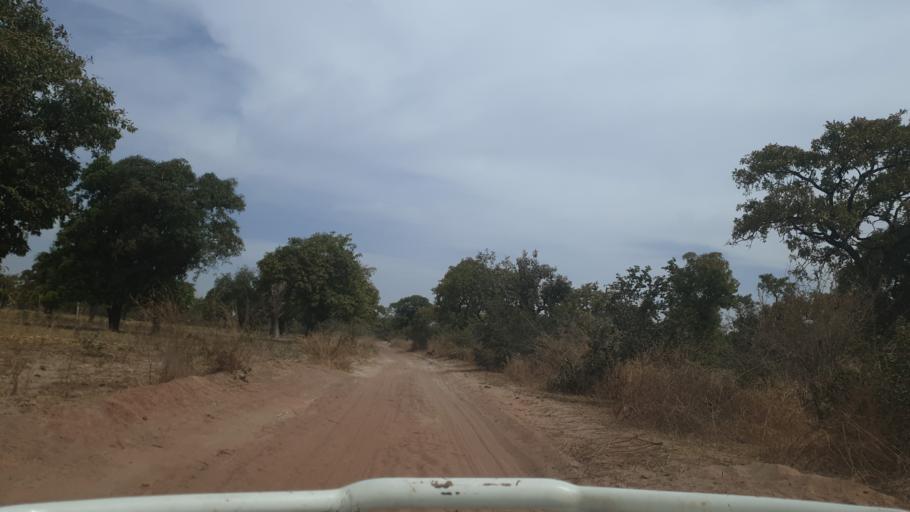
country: ML
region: Sikasso
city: Yorosso
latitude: 12.2325
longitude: -4.7472
